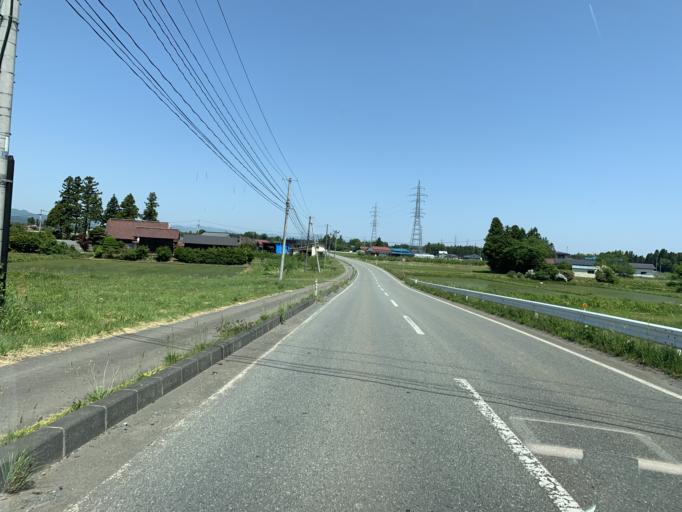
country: JP
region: Iwate
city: Mizusawa
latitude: 39.1756
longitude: 141.0817
